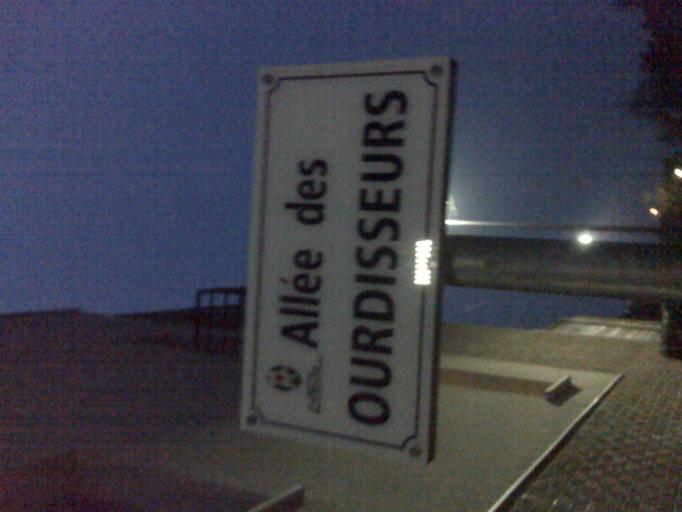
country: FR
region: Nord-Pas-de-Calais
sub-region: Departement du Nord
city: Linselles
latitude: 50.7343
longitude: 3.0723
